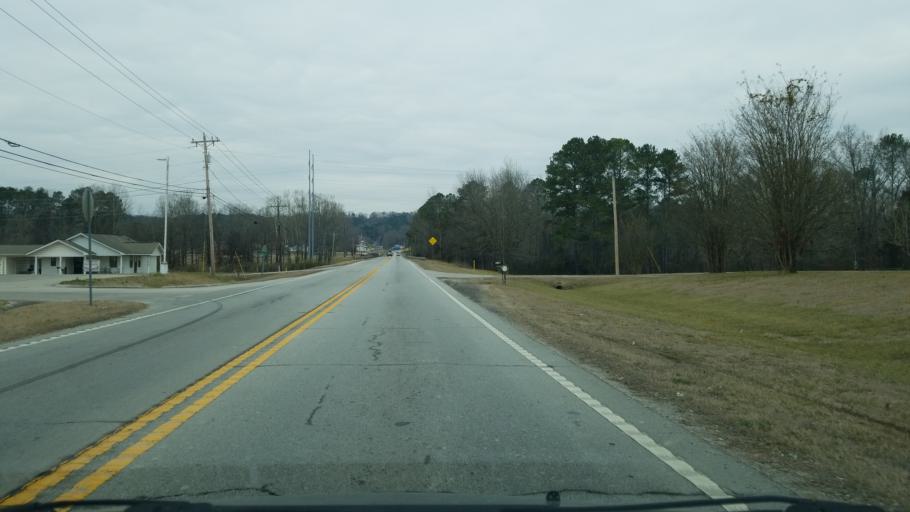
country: US
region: Georgia
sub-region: Catoosa County
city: Indian Springs
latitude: 34.9635
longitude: -85.1740
